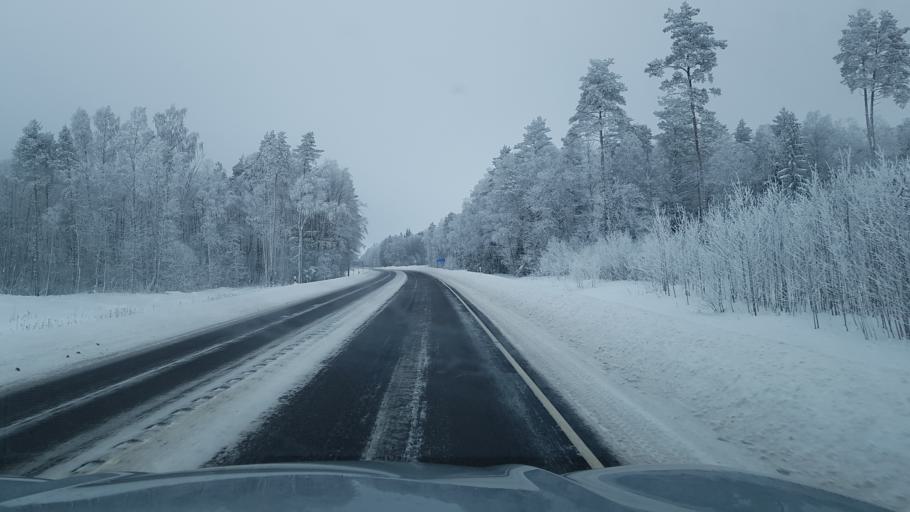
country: EE
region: Ida-Virumaa
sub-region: Johvi vald
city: Johvi
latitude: 59.2929
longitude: 27.3991
